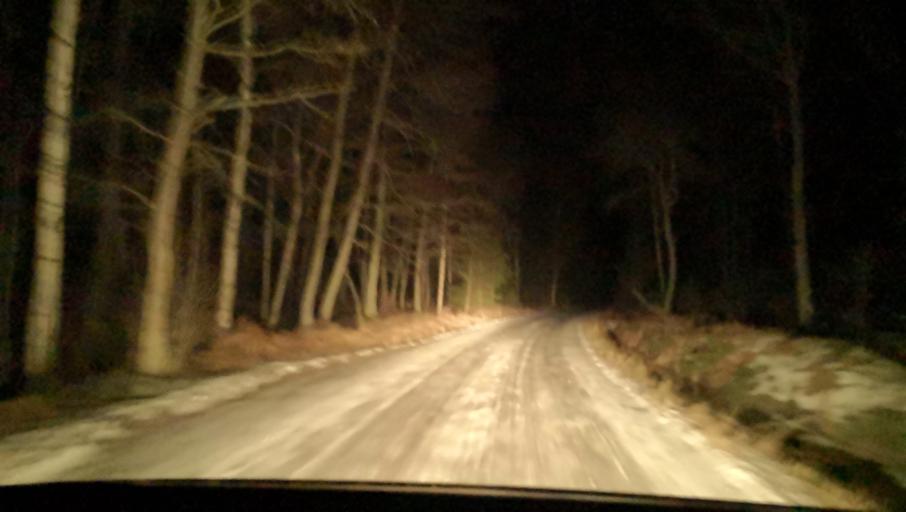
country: SE
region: Stockholm
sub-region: Nacka Kommun
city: Fisksatra
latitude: 59.2772
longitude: 18.2325
